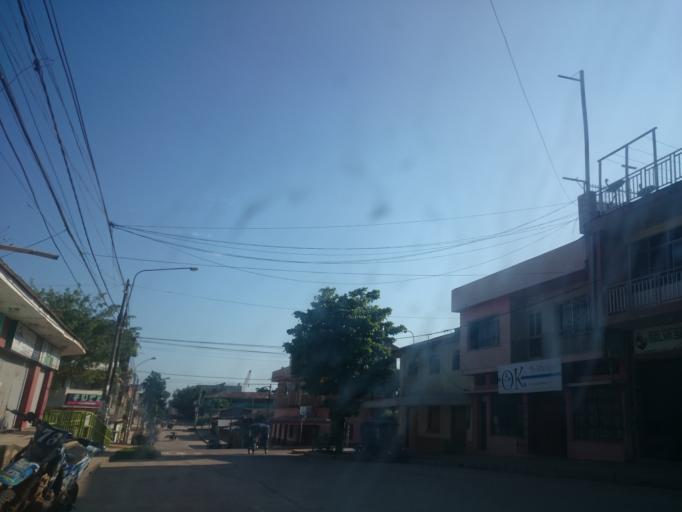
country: PE
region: Ucayali
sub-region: Provincia de Coronel Portillo
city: Pucallpa
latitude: -8.3843
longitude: -74.5285
